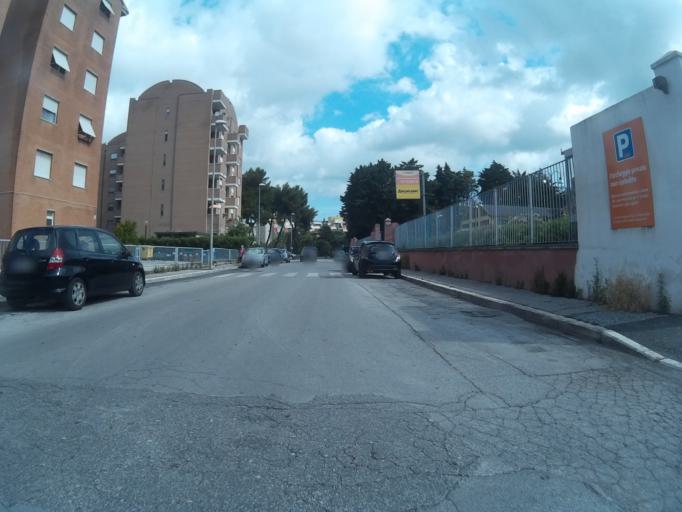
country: IT
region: Tuscany
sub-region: Provincia di Livorno
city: Livorno
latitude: 43.5630
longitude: 10.3228
